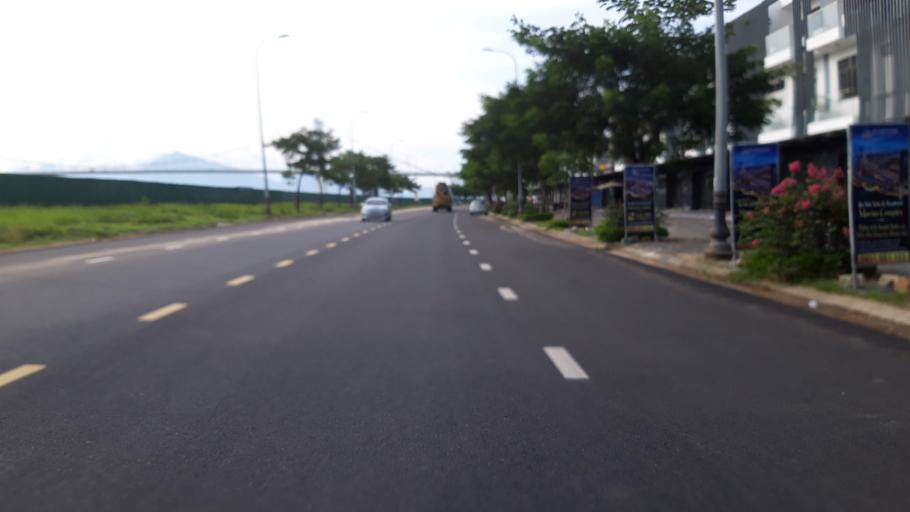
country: VN
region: Da Nang
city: Da Nang
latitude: 16.0912
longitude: 108.2264
